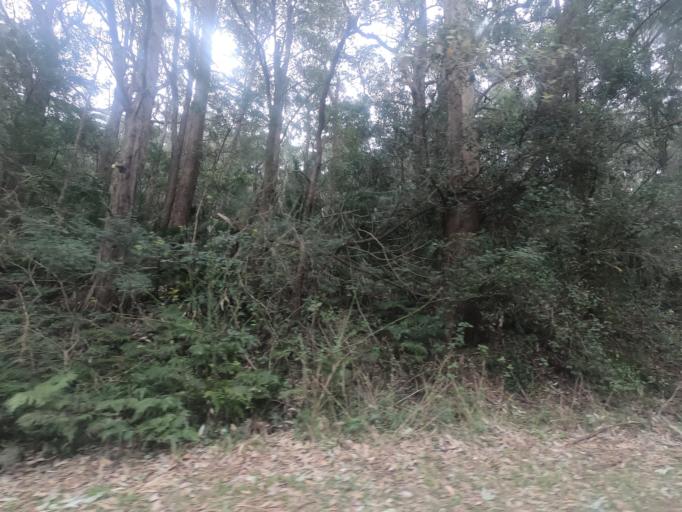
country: AU
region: New South Wales
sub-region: Wollongong
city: Bulli
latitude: -34.3011
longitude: 150.9287
